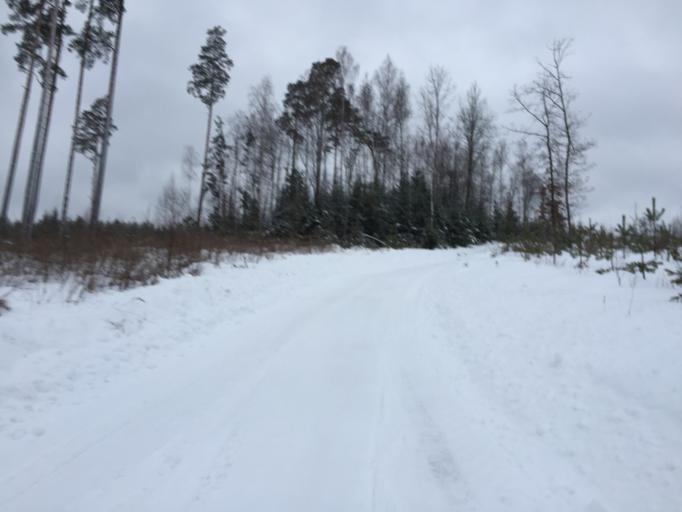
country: LV
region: Amatas Novads
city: Drabesi
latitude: 57.1970
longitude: 25.2951
